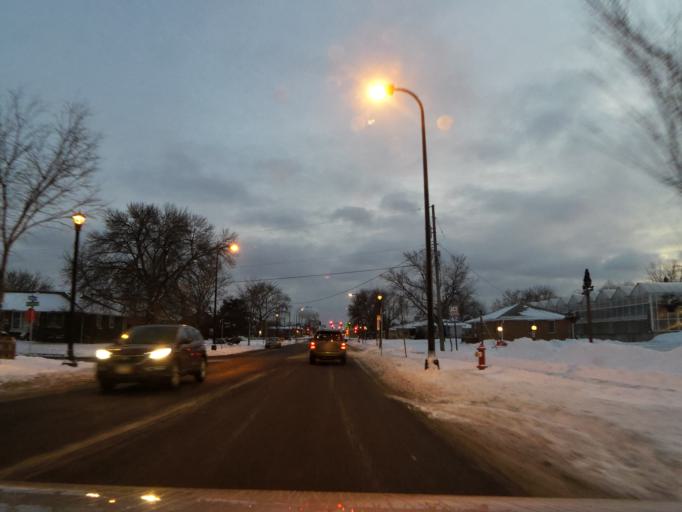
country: US
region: Minnesota
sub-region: Hennepin County
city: Richfield
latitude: 44.8929
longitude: -93.3087
